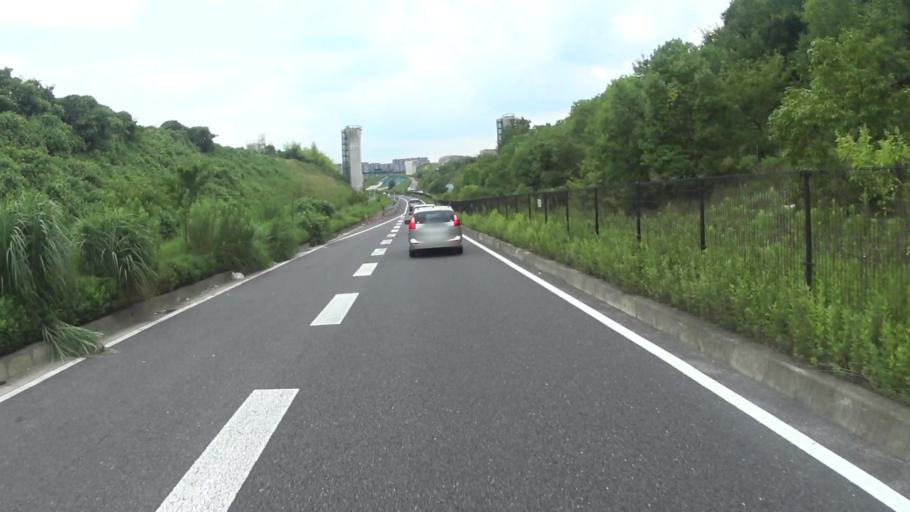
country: JP
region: Kyoto
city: Yawata
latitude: 34.8458
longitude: 135.7261
